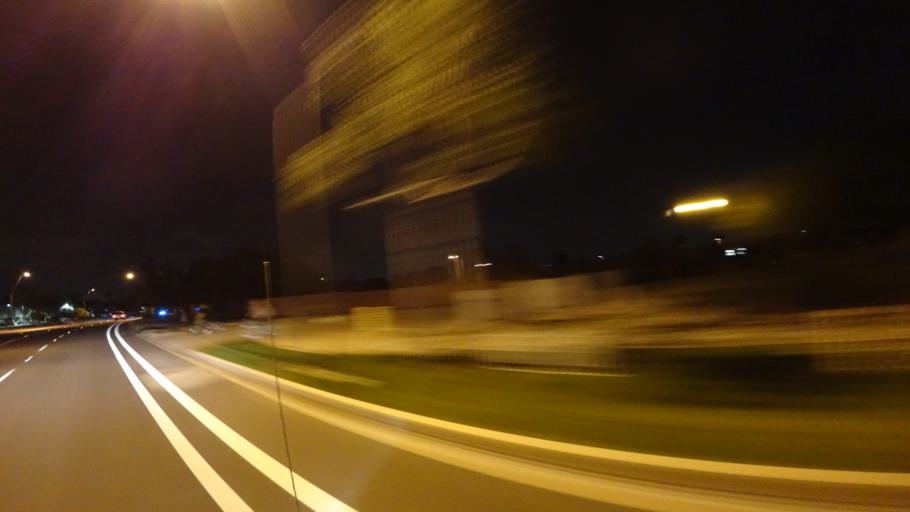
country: US
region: Arizona
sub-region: Maricopa County
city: Guadalupe
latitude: 33.3540
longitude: -111.9575
